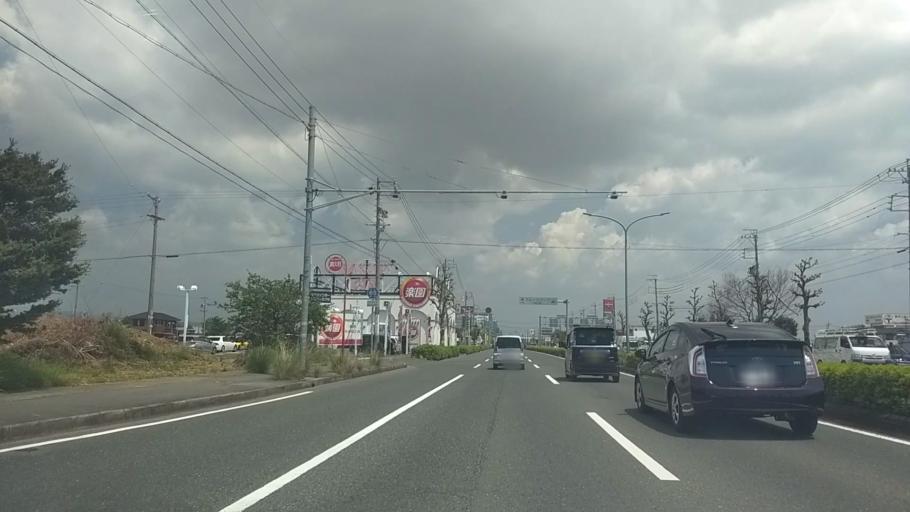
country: JP
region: Shizuoka
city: Hamamatsu
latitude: 34.7623
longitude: 137.6828
